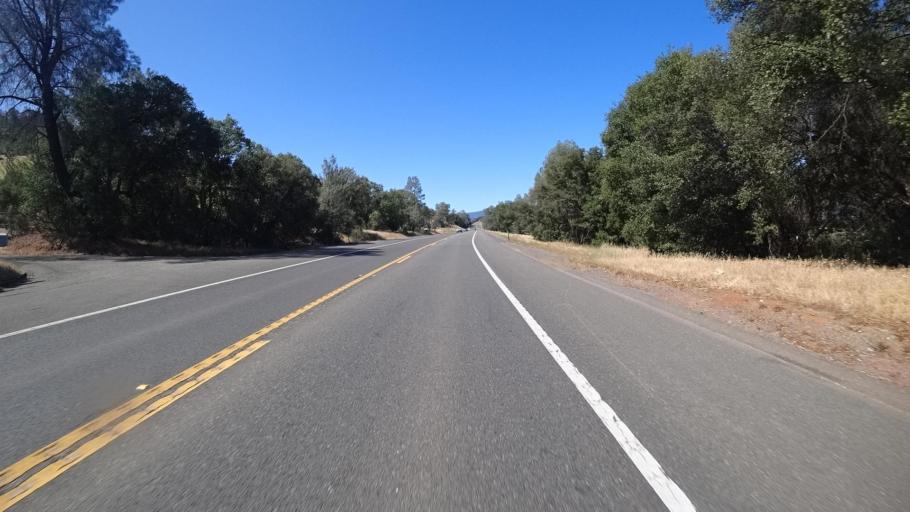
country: US
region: California
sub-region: Lake County
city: Clearlake
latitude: 38.9693
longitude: -122.6139
